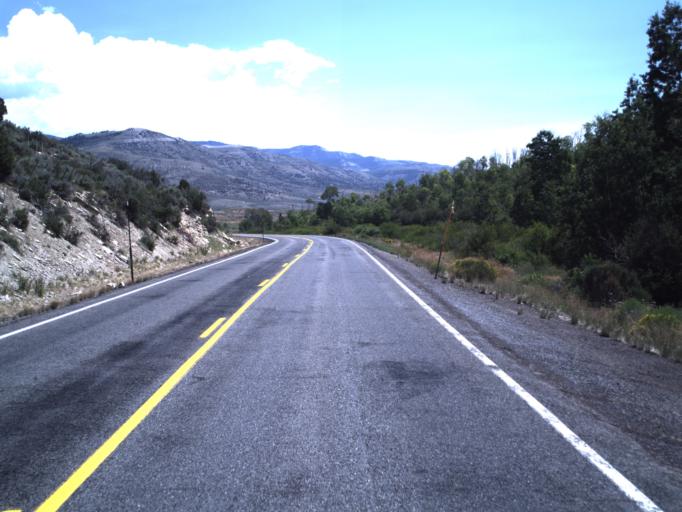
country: US
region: Utah
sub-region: Carbon County
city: Helper
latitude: 39.8576
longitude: -111.0576
